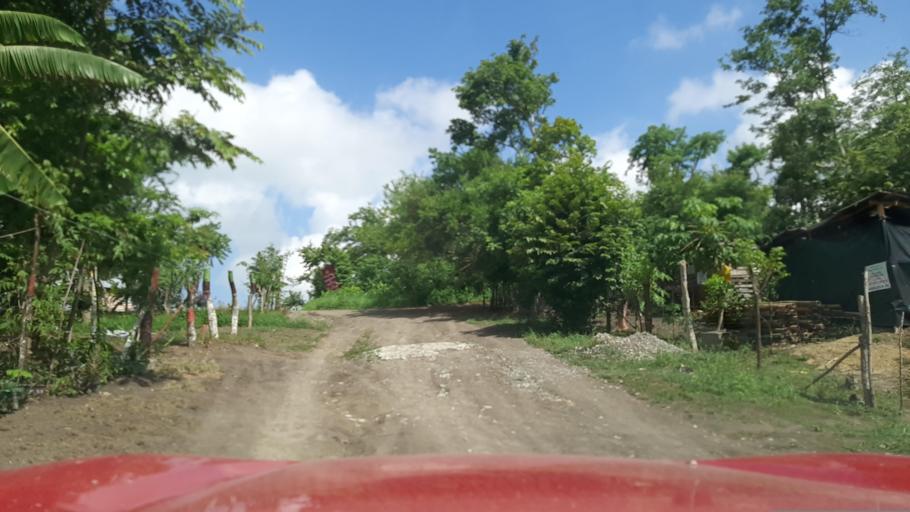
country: MX
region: Veracruz
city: Coatzintla
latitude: 20.5038
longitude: -97.4608
